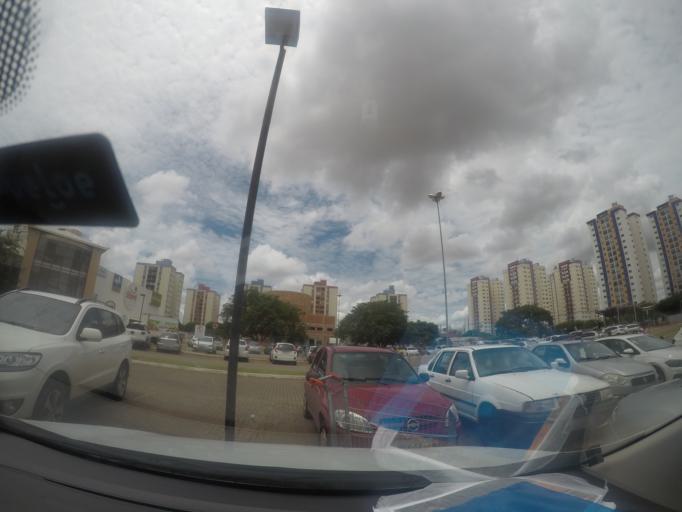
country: BR
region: Goias
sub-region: Goiania
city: Goiania
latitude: -16.7081
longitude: -49.3283
